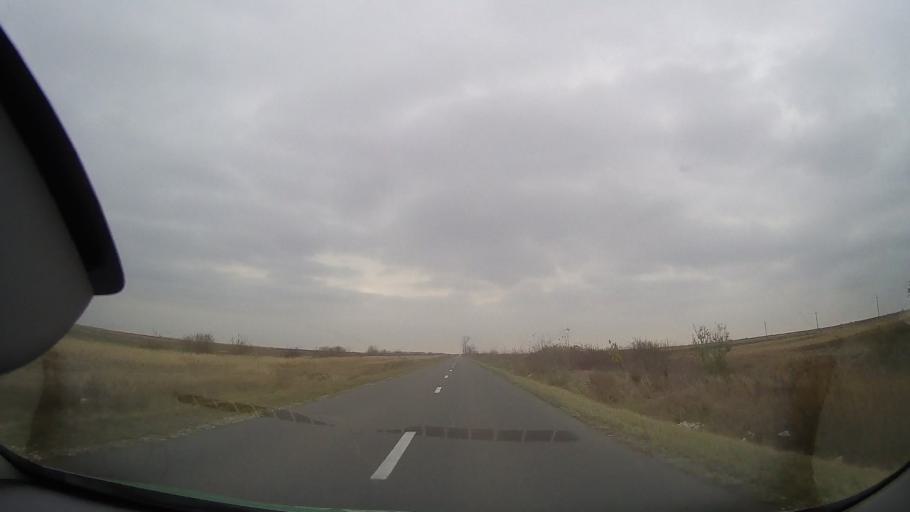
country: RO
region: Ialomita
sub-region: Comuna Garbovi
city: Garbovi
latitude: 44.7652
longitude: 26.7373
